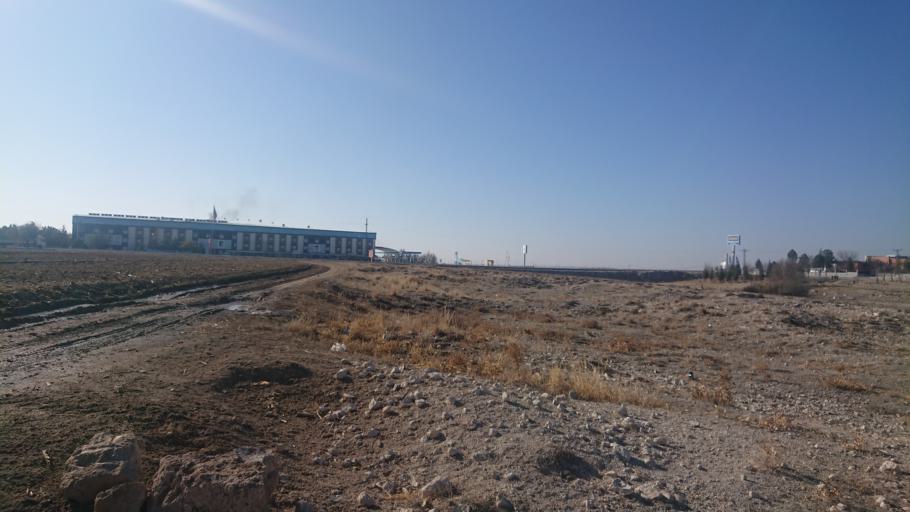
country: TR
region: Aksaray
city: Sultanhani
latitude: 38.2542
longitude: 33.5084
